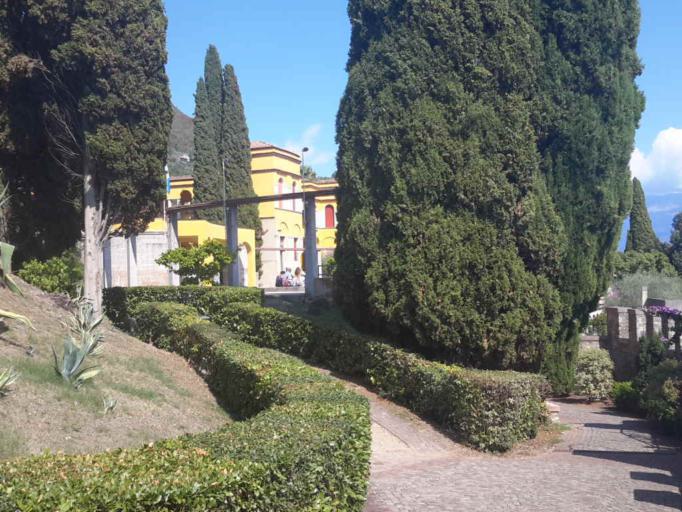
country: IT
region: Lombardy
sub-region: Provincia di Brescia
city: Gardone Riviera
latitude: 45.6238
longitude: 10.5646
